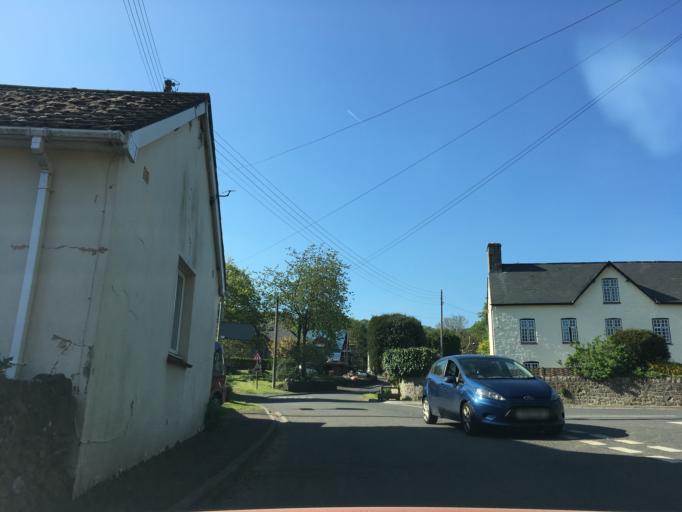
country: GB
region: Wales
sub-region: Newport
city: Llanvaches
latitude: 51.6266
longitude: -2.7990
